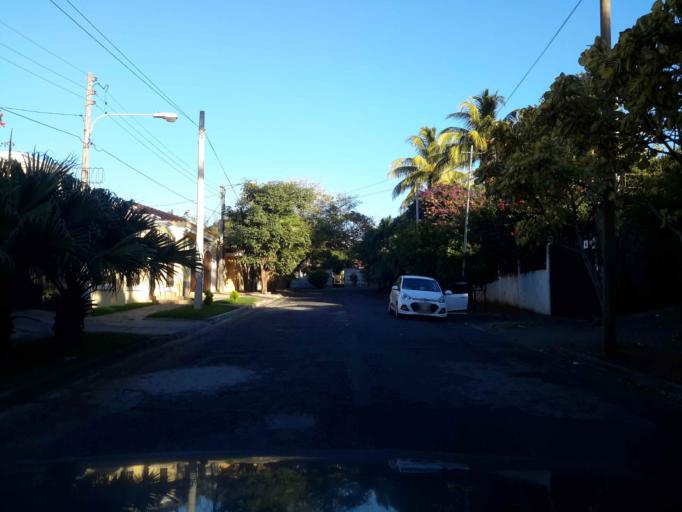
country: NI
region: Managua
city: Managua
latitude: 12.1020
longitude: -86.2667
